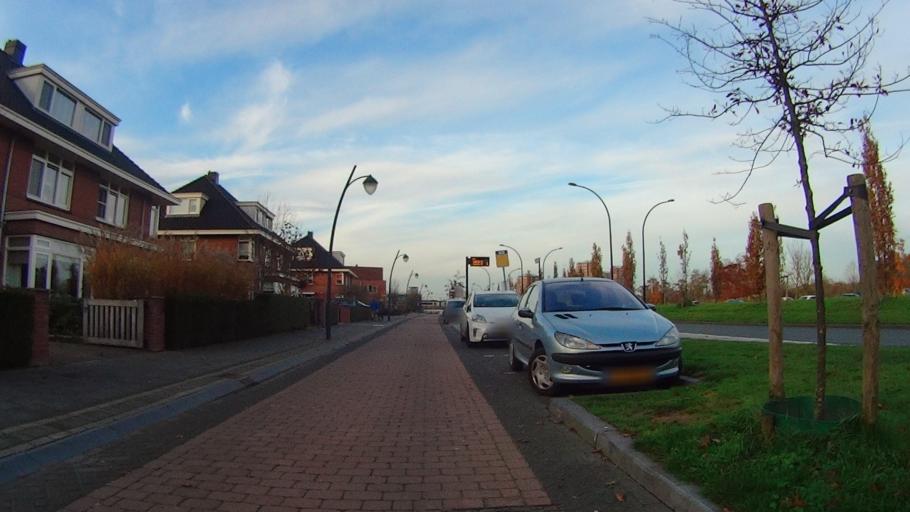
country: NL
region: Utrecht
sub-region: Gemeente Amersfoort
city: Randenbroek
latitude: 52.1907
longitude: 5.4348
